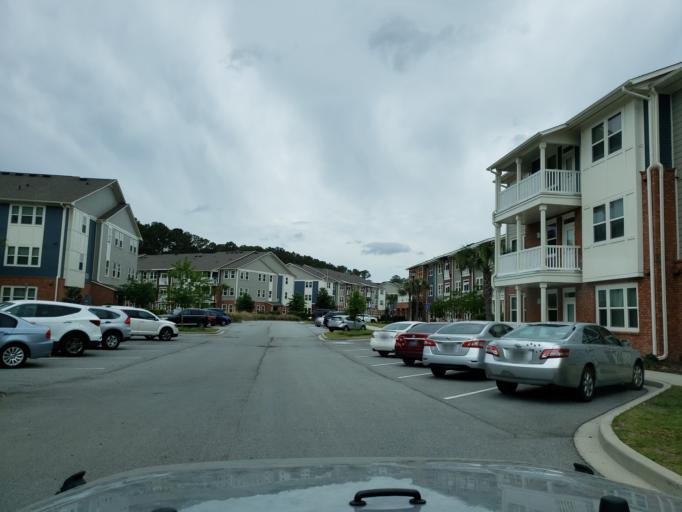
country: US
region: Georgia
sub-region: Chatham County
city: Pooler
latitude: 32.1743
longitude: -81.2287
